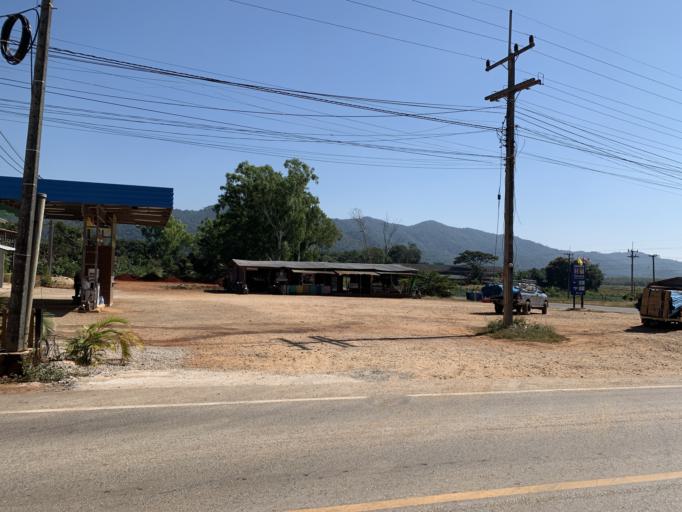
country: TH
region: Tak
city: Phop Phra
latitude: 16.4755
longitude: 98.8358
